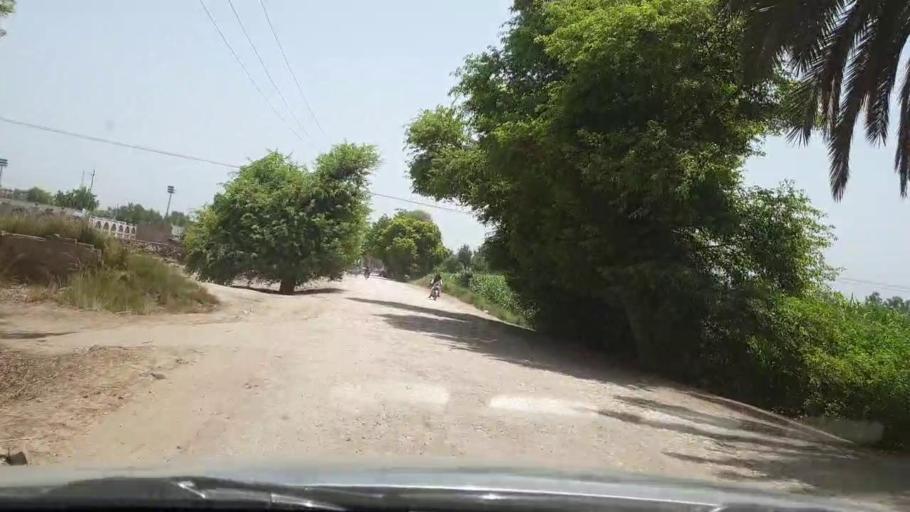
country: PK
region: Sindh
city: Pano Aqil
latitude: 27.8575
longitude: 69.0997
